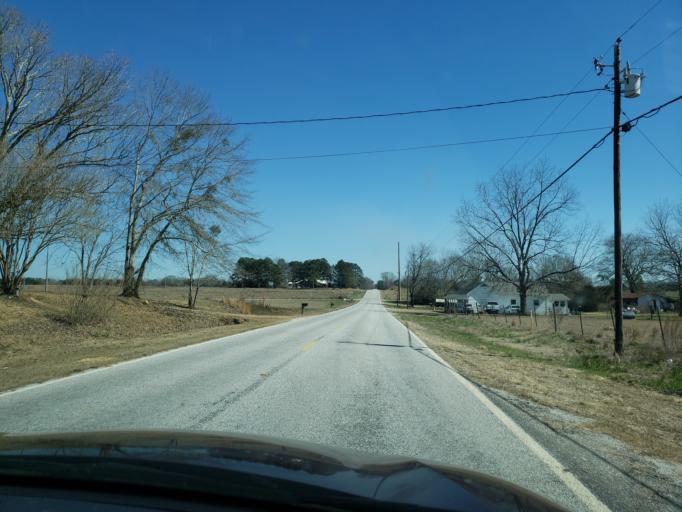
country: US
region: Alabama
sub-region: Elmore County
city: Tallassee
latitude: 32.5813
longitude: -85.7662
